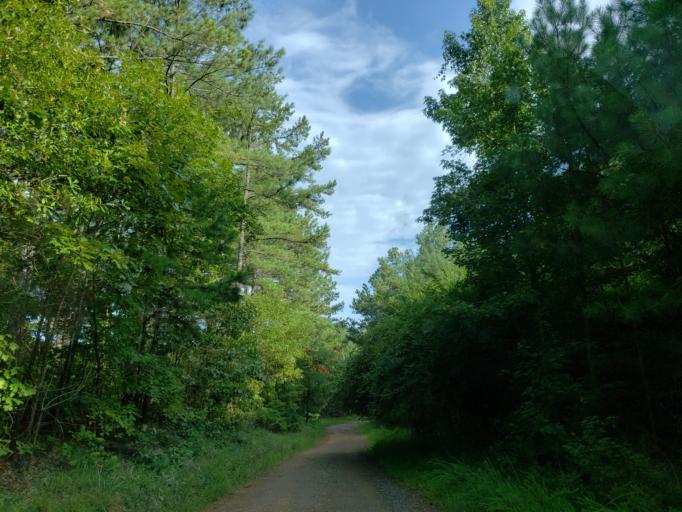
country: US
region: Georgia
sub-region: Bartow County
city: Emerson
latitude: 34.1867
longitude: -84.6470
